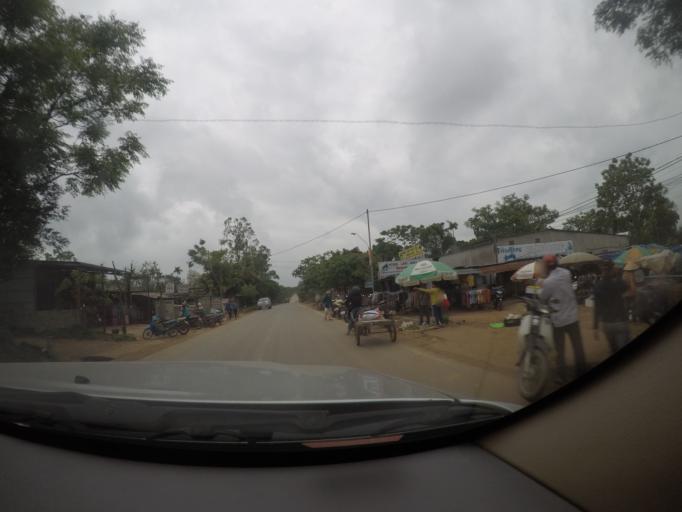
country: VN
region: Quang Tri
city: Cam Lo
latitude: 16.8841
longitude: 106.9928
